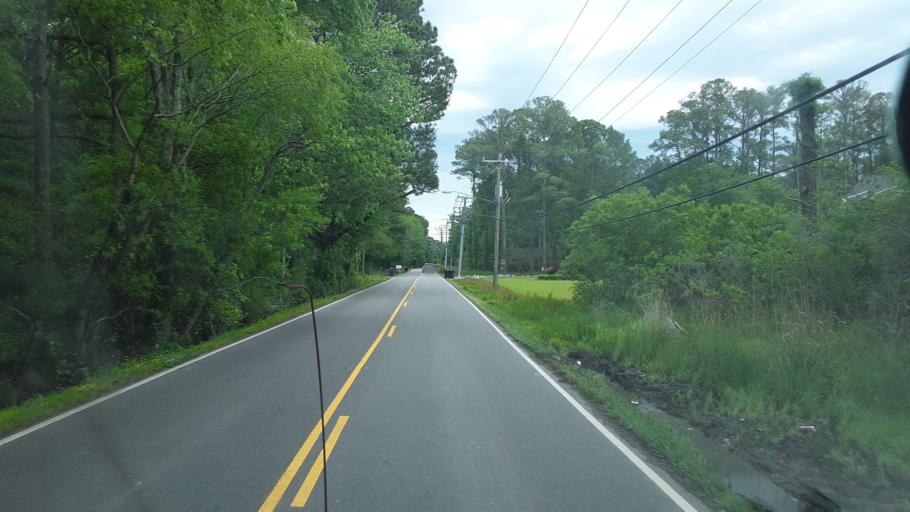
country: US
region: Virginia
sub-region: City of Virginia Beach
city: Virginia Beach
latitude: 36.7406
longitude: -75.9692
